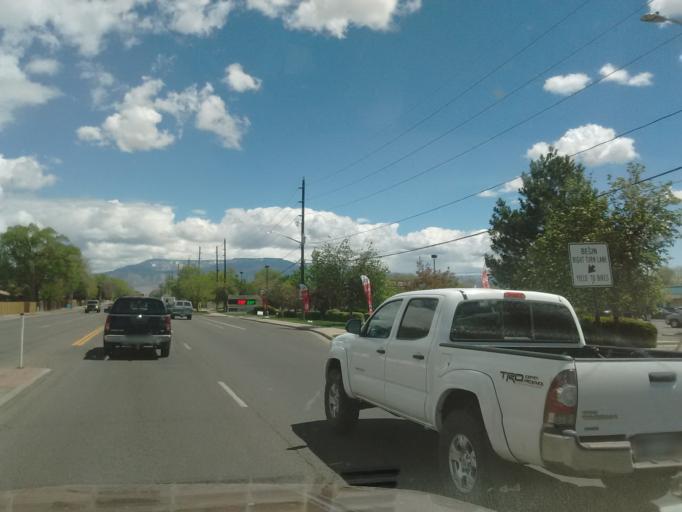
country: US
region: Colorado
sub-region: Mesa County
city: Fruitvale
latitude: 39.0918
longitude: -108.5142
